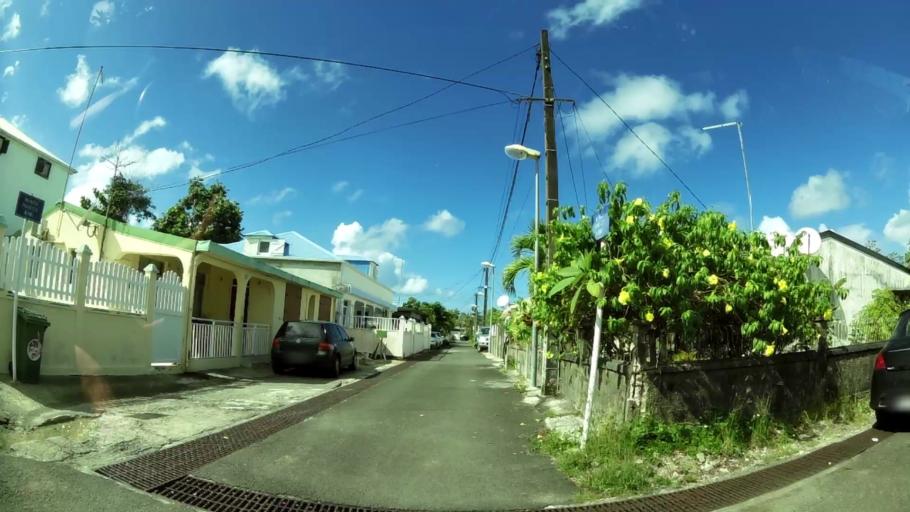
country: GP
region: Guadeloupe
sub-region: Guadeloupe
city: Port-Louis
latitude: 16.4205
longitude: -61.5298
